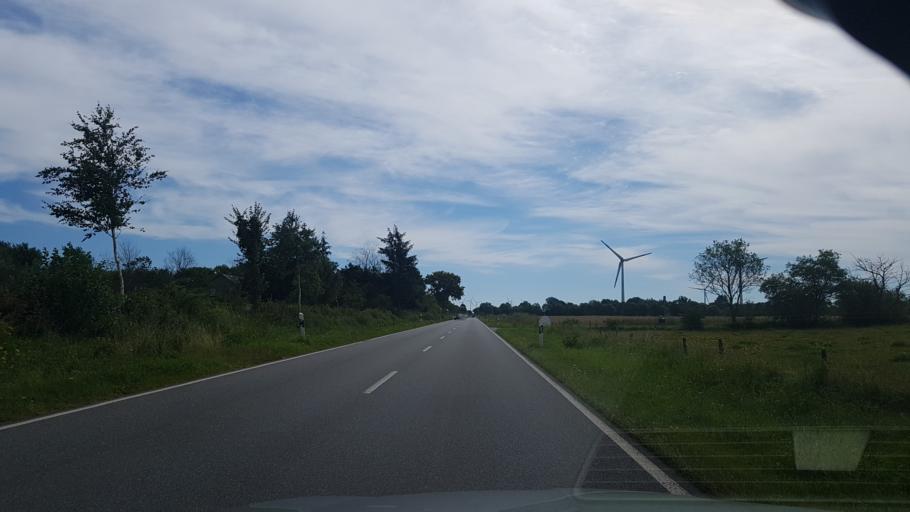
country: DE
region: Schleswig-Holstein
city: Weesby
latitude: 54.8640
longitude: 9.1147
